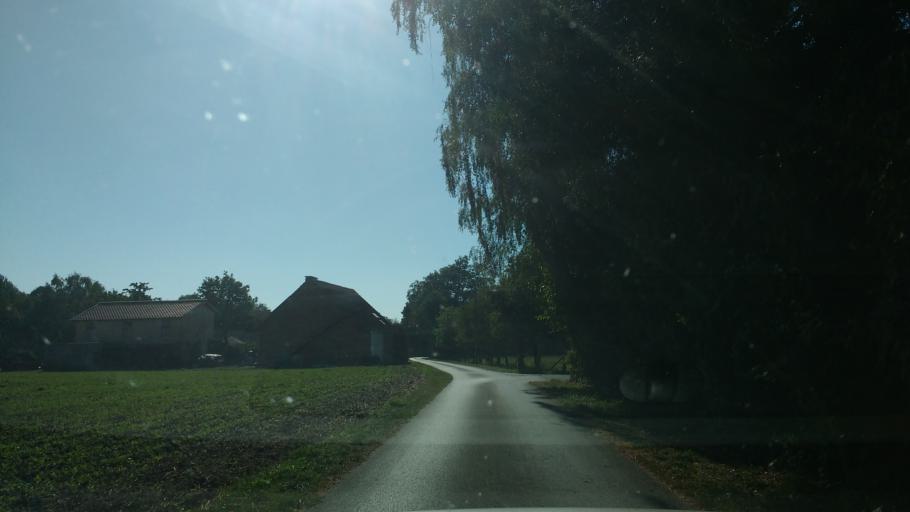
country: DE
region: North Rhine-Westphalia
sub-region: Regierungsbezirk Detmold
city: Delbruck
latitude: 51.7569
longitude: 8.5398
